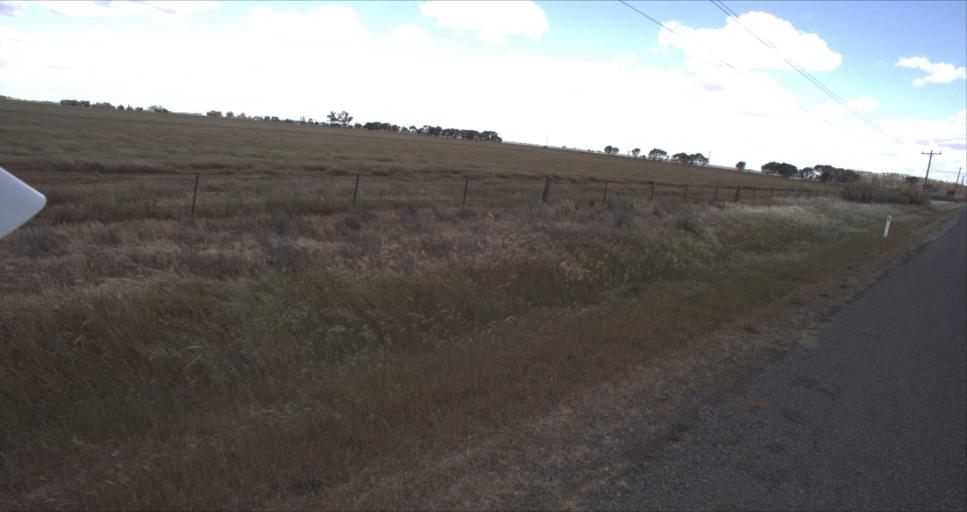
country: AU
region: New South Wales
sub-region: Leeton
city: Leeton
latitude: -34.5276
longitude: 146.2201
